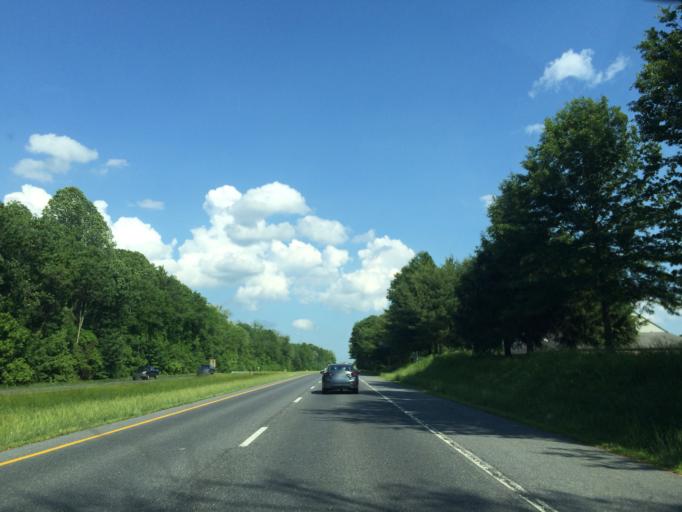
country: US
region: Maryland
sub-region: Howard County
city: Columbia
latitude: 39.2858
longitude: -76.8812
